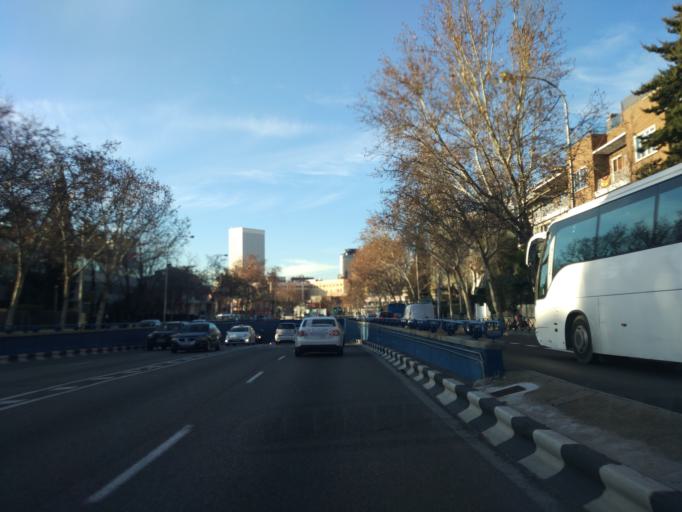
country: ES
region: Madrid
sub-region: Provincia de Madrid
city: Salamanca
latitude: 40.4438
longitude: -3.6839
